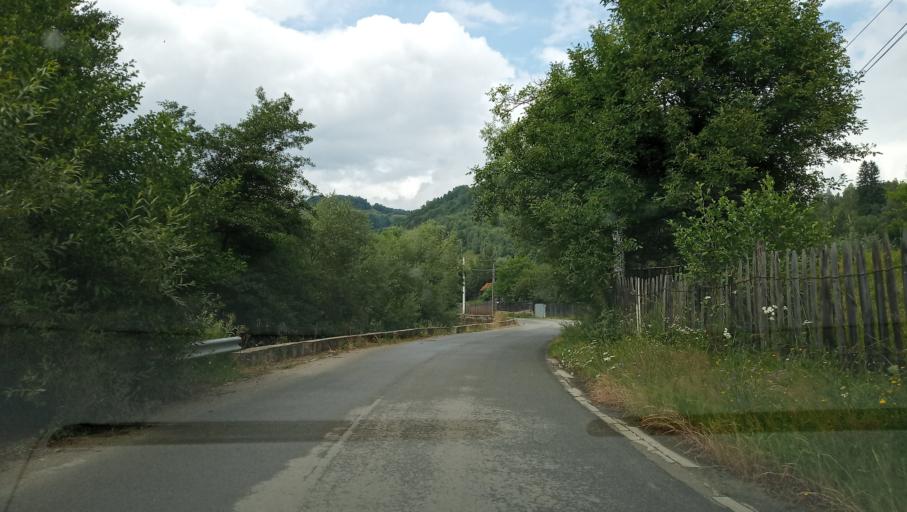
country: RO
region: Hunedoara
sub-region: Oras Petrila
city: Petrila
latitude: 45.4566
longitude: 23.4181
